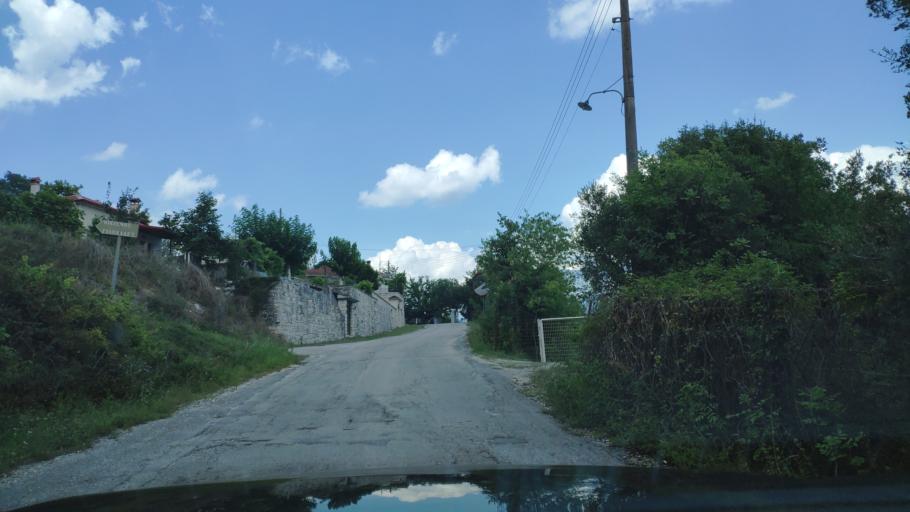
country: GR
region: Epirus
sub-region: Nomos Artas
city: Agios Dimitrios
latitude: 39.4439
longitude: 21.0160
